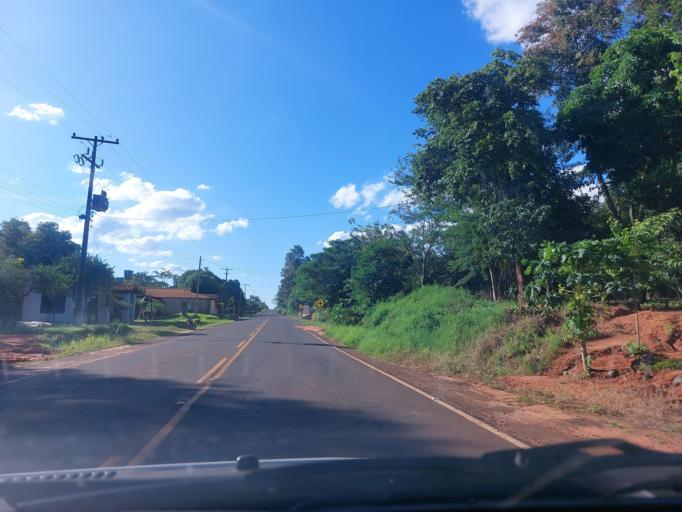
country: PY
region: San Pedro
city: Guayaybi
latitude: -24.5872
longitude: -56.5196
